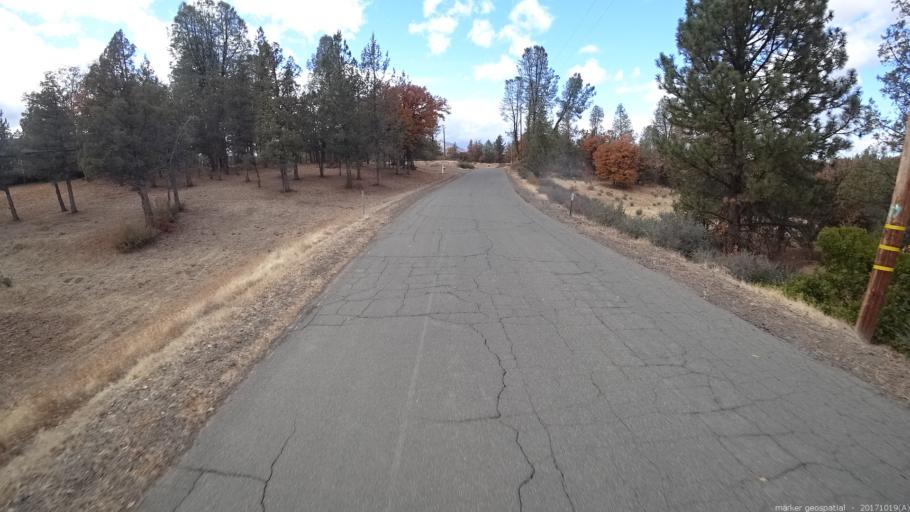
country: US
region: California
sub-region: Shasta County
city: Burney
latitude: 40.9766
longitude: -121.4430
